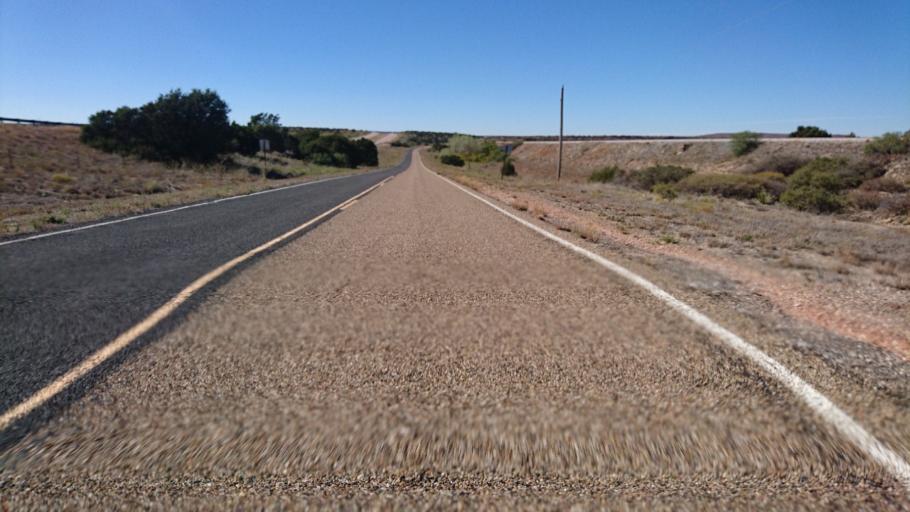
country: US
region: New Mexico
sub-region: Quay County
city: Tucumcari
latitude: 35.0689
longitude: -104.2049
